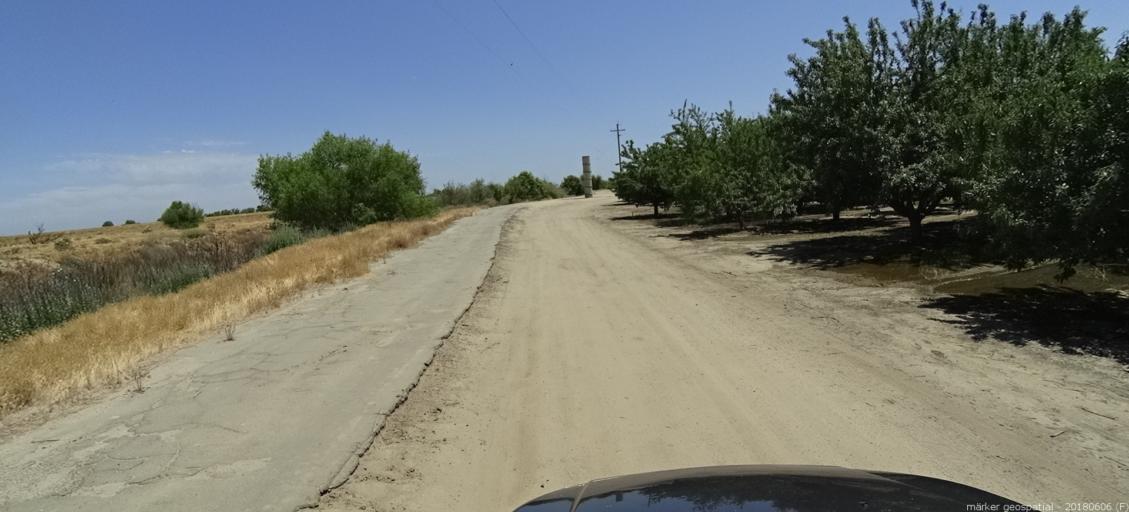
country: US
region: California
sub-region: Fresno County
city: Mendota
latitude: 36.7862
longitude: -120.3033
